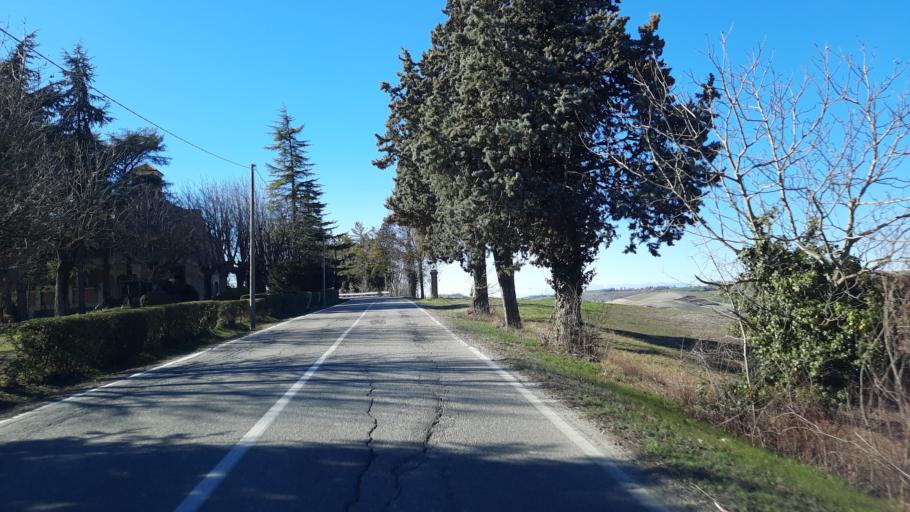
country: IT
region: Piedmont
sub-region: Provincia di Alessandria
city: San Giorgio Monferrato
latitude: 45.0921
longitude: 8.4242
